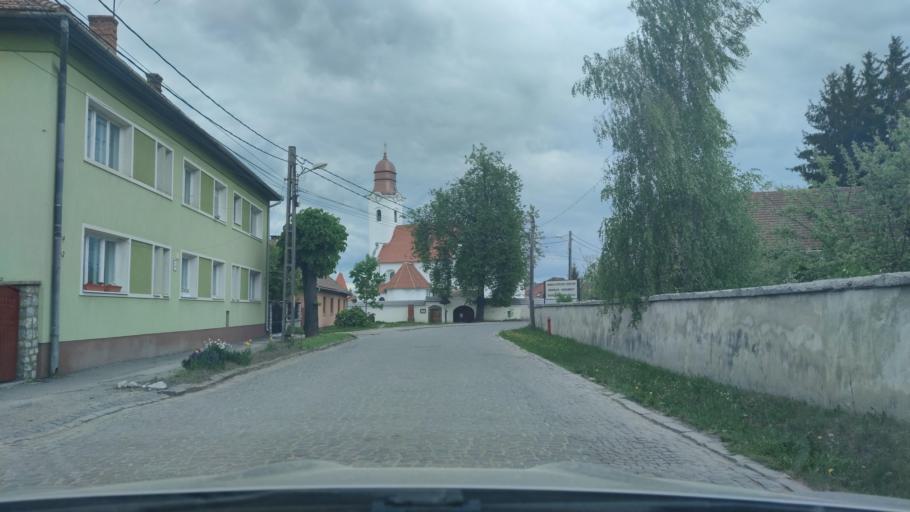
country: RO
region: Harghita
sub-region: Municipiul Gheorgheni
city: Gheorgheni
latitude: 46.7238
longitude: 25.6066
